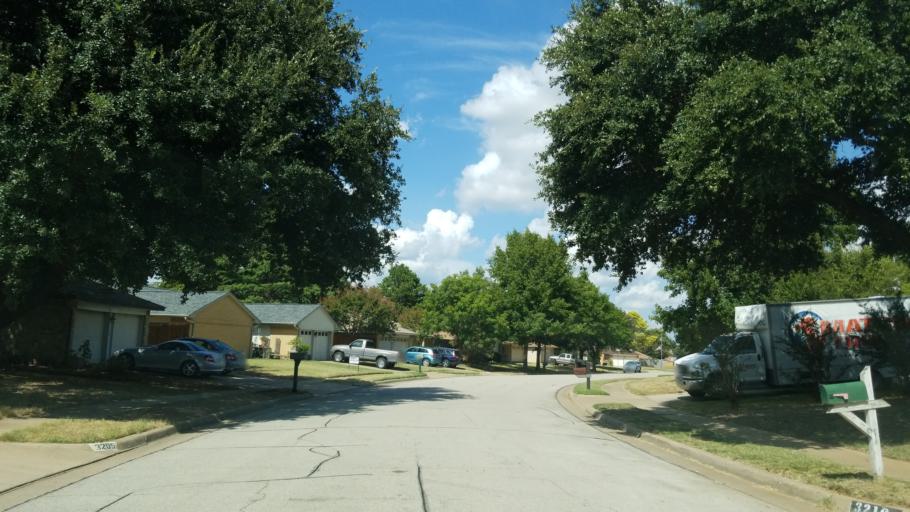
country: US
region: Texas
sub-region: Tarrant County
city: Bedford
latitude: 32.8576
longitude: -97.1107
